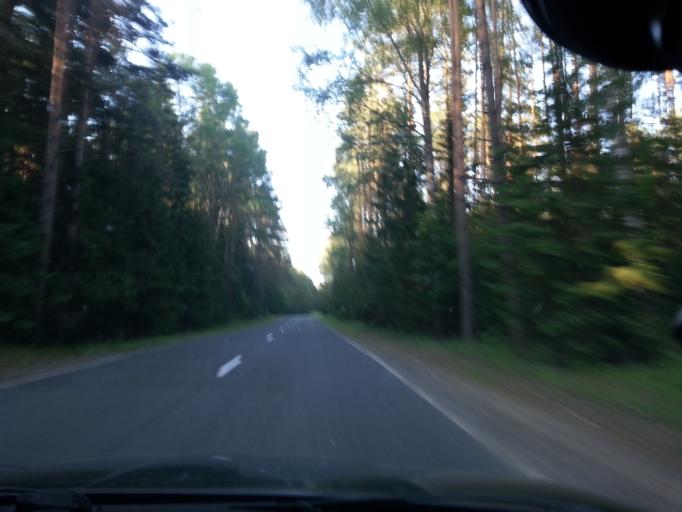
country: BY
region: Minsk
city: Narach
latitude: 54.9443
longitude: 26.5770
